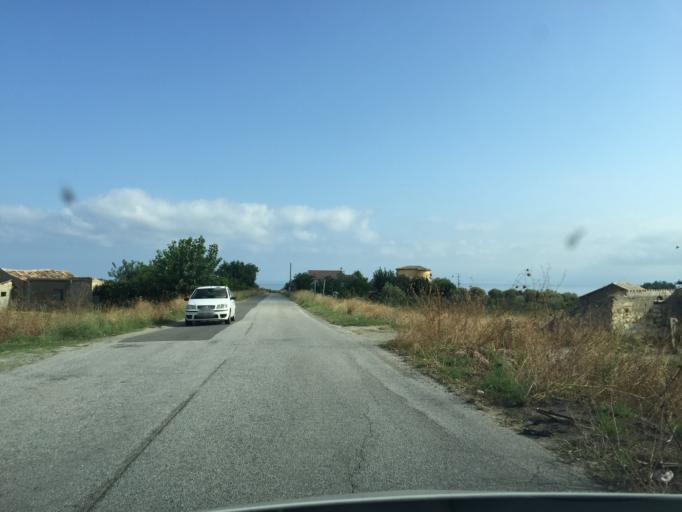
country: IT
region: Calabria
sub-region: Provincia di Vibo-Valentia
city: Pannaconi
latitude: 38.7110
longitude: 16.0491
